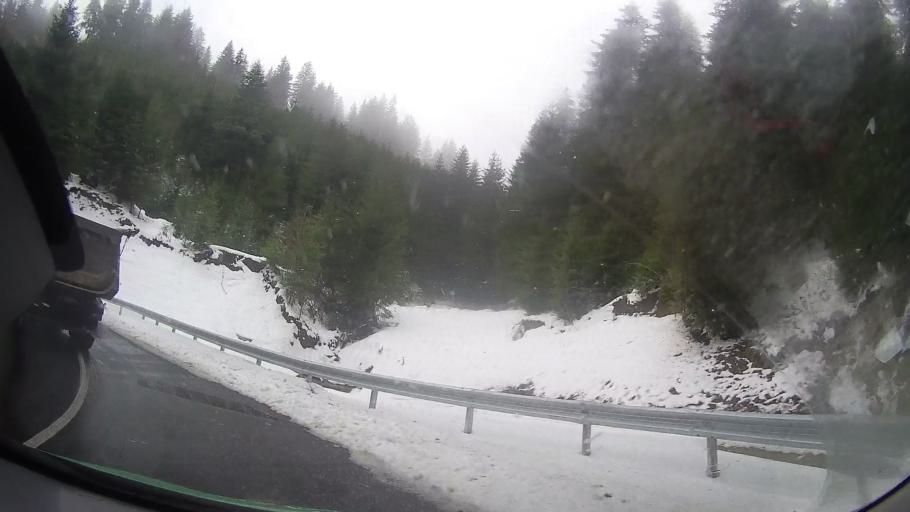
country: RO
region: Harghita
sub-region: Oras Balan
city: Balan
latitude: 46.7785
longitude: 25.7427
